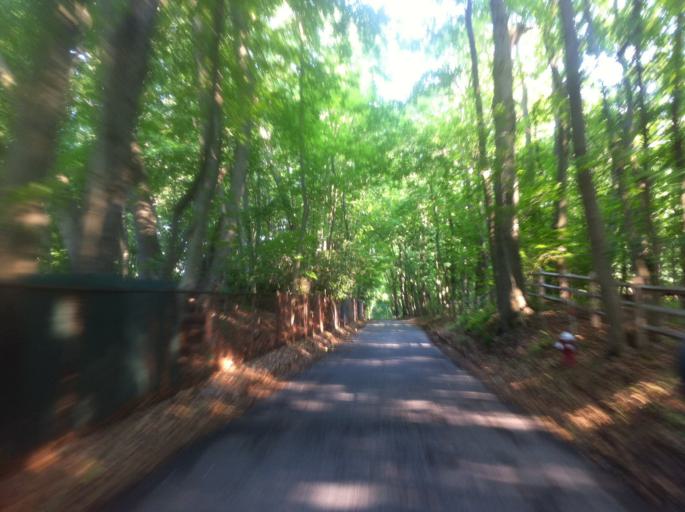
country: US
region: New York
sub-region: Nassau County
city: Lattingtown
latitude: 40.9017
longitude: -73.5917
